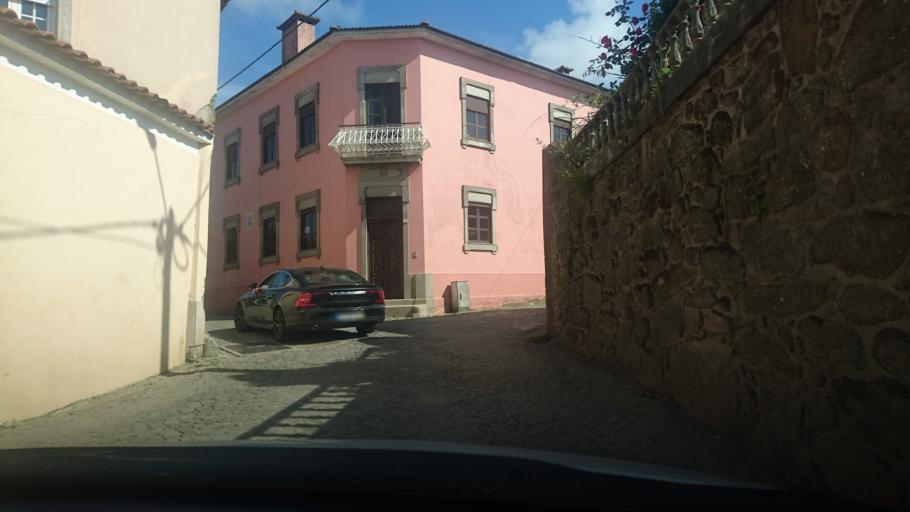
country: PT
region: Porto
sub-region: Matosinhos
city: Lavra
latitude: 41.2671
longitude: -8.7110
